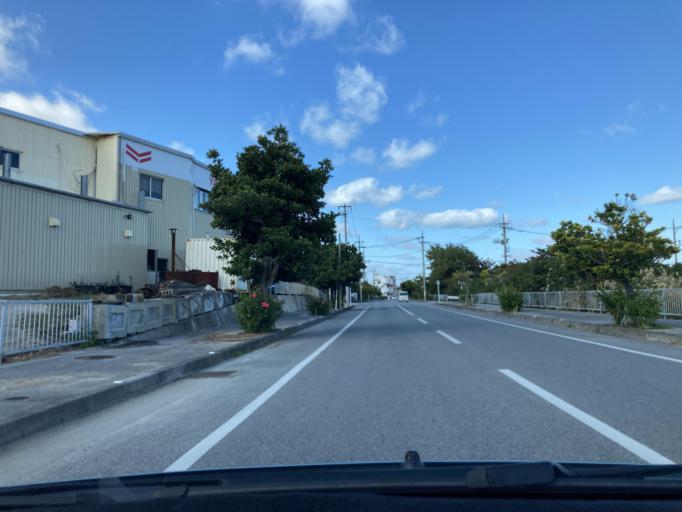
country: JP
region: Okinawa
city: Katsuren-haebaru
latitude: 26.3066
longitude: 127.9208
